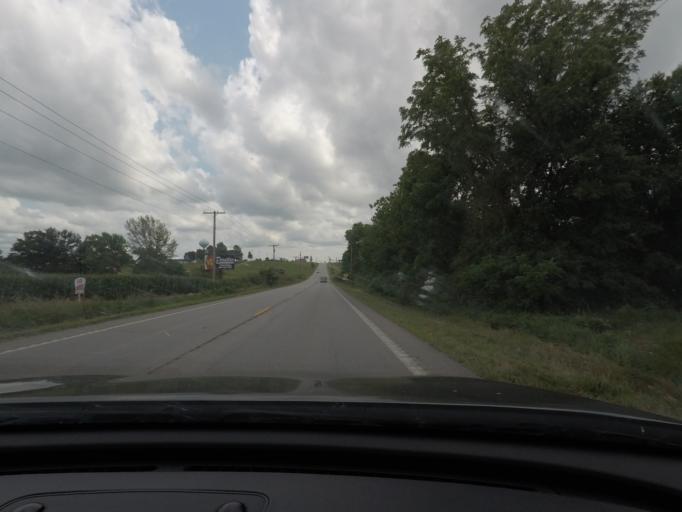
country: US
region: Missouri
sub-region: Lafayette County
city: Higginsville
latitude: 39.0094
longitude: -93.7351
